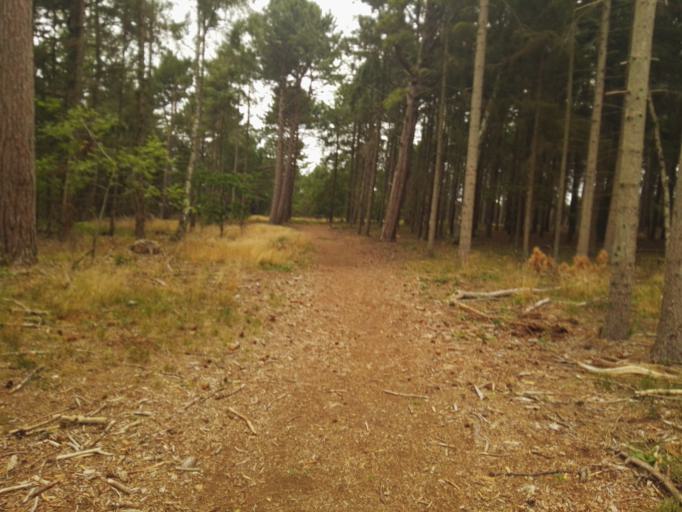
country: DK
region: Zealand
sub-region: Odsherred Kommune
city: Nykobing Sjaelland
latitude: 55.9428
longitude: 11.6817
